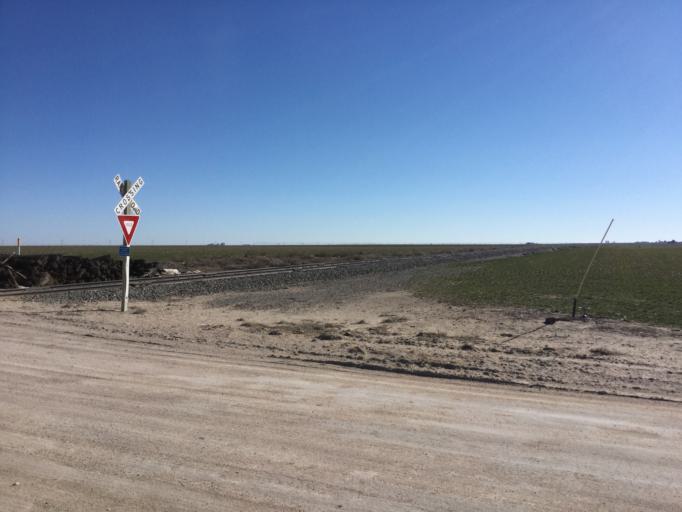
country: US
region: Kansas
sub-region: Wichita County
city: Leoti
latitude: 38.4847
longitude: -101.4763
